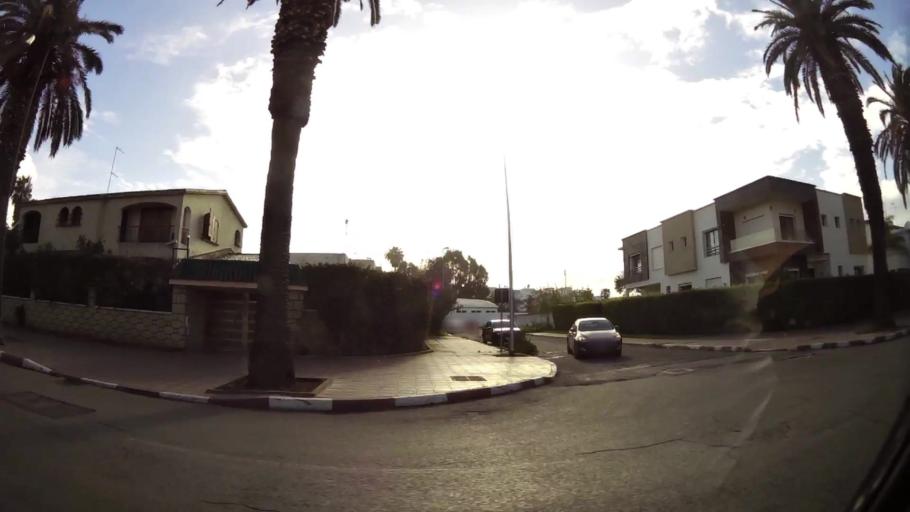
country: MA
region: Grand Casablanca
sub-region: Mohammedia
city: Mohammedia
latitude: 33.7018
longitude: -7.3940
